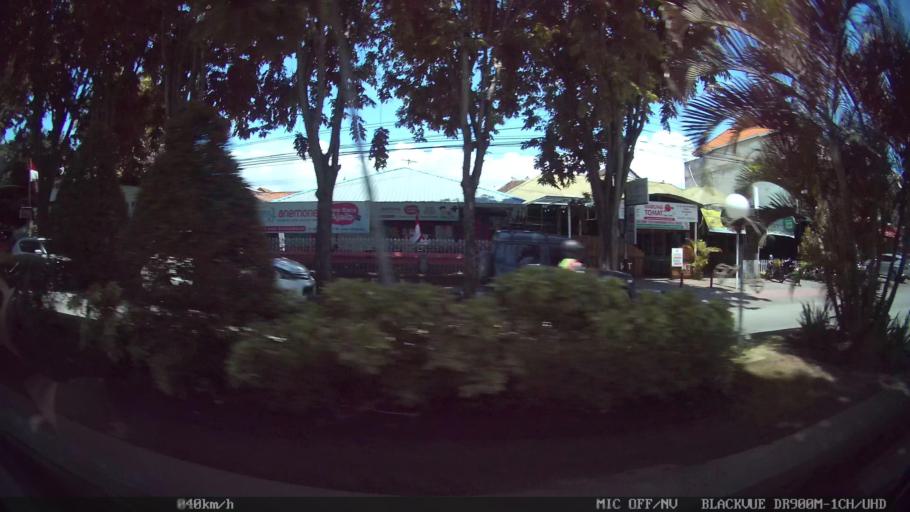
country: ID
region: Bali
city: Singaraja
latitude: -8.1155
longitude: 115.0890
